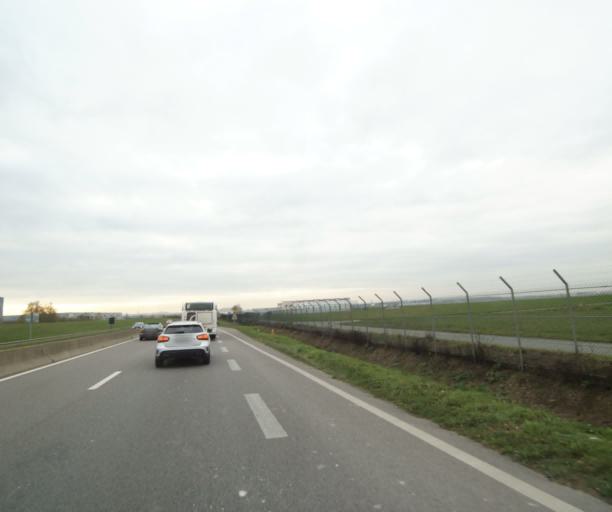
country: FR
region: Ile-de-France
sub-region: Departement du Val-d'Oise
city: Gonesse
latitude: 48.9706
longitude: 2.4578
